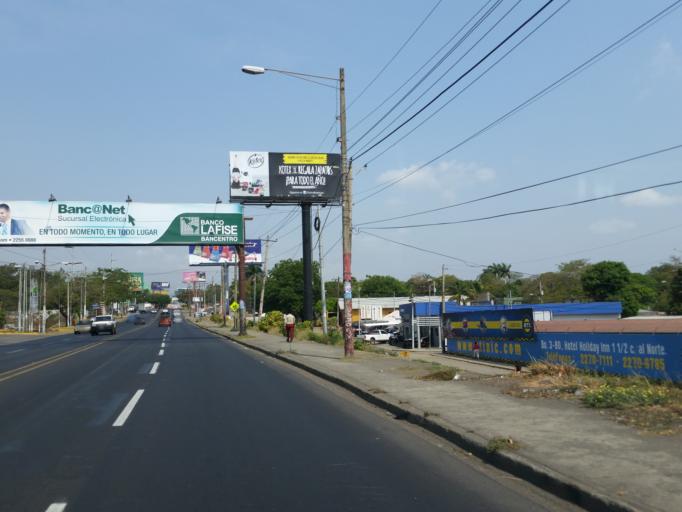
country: NI
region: Managua
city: Managua
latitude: 12.1249
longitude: -86.2790
